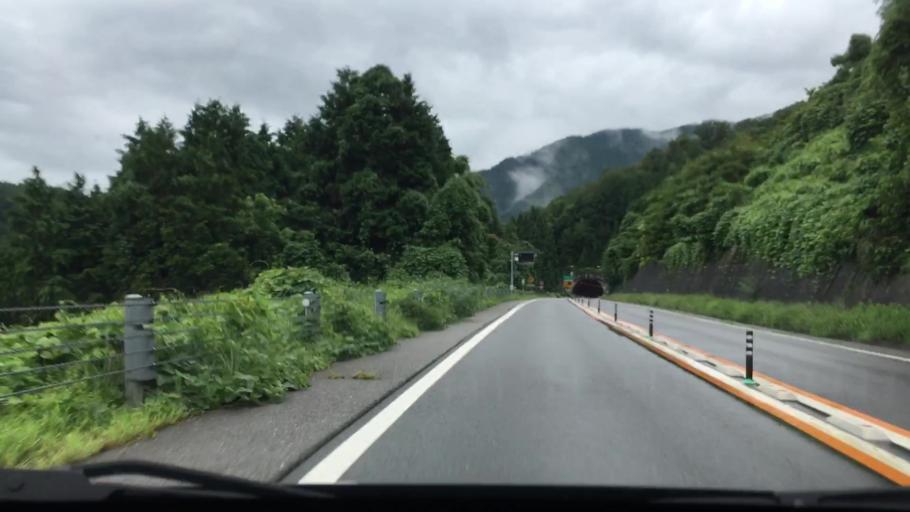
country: JP
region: Hyogo
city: Toyooka
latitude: 35.2436
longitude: 134.7887
